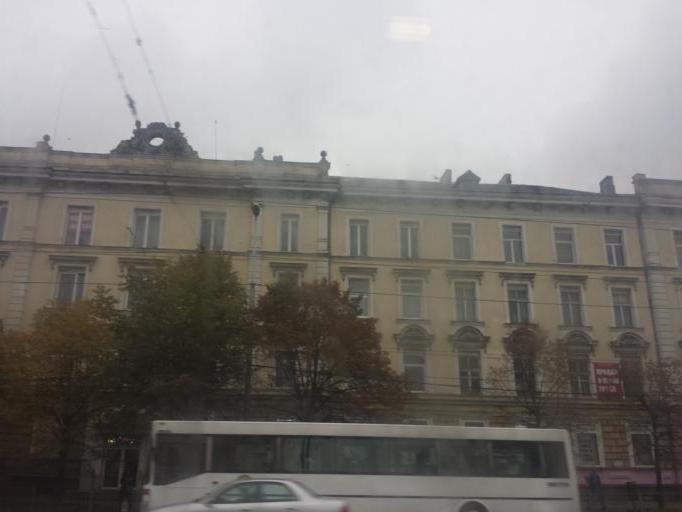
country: RU
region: Kaliningrad
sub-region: Gorod Kaliningrad
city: Kaliningrad
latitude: 54.7007
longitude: 20.5039
